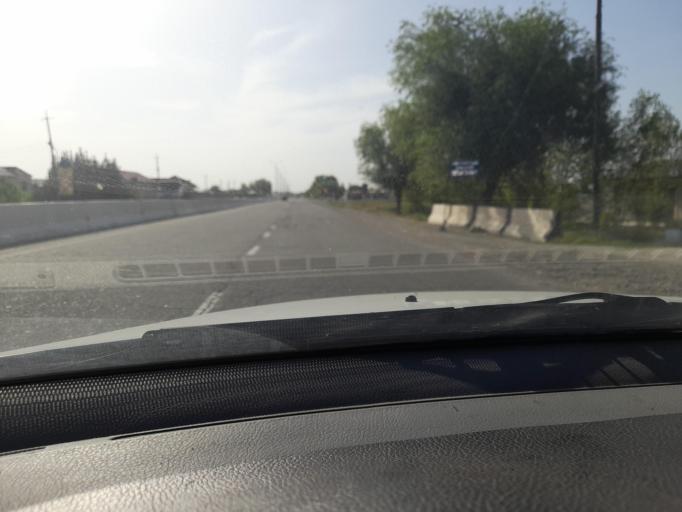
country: UZ
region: Samarqand
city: Kattaqo'rg'on
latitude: 39.9211
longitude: 66.2915
